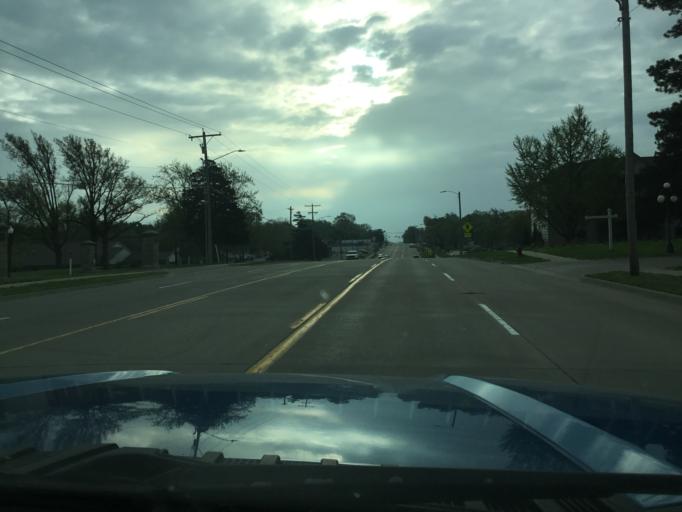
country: US
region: Kansas
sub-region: Shawnee County
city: Topeka
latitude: 39.0585
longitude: -95.7216
